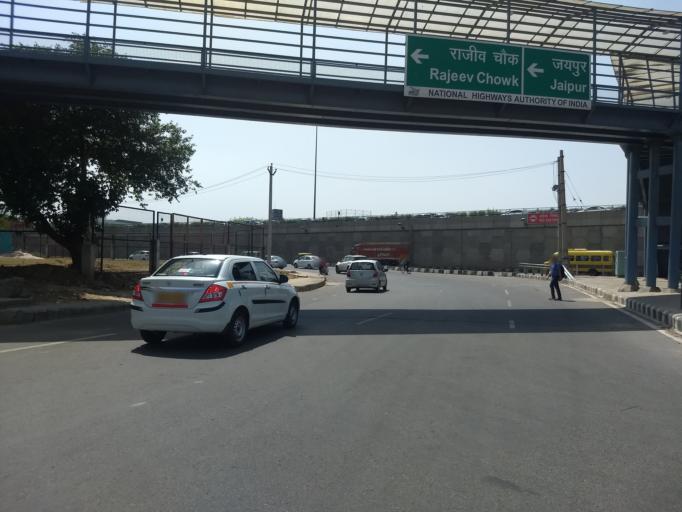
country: IN
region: Haryana
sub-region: Gurgaon
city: Gurgaon
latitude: 28.4681
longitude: 77.0578
